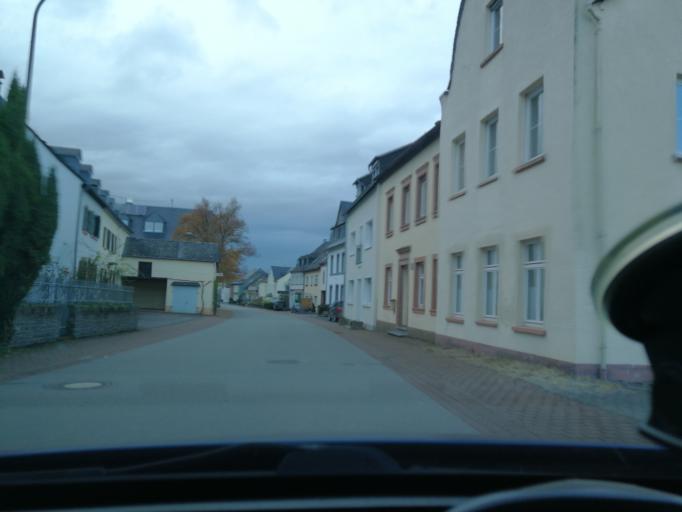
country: DE
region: Rheinland-Pfalz
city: Osann-Monzel
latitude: 49.9096
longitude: 6.9558
